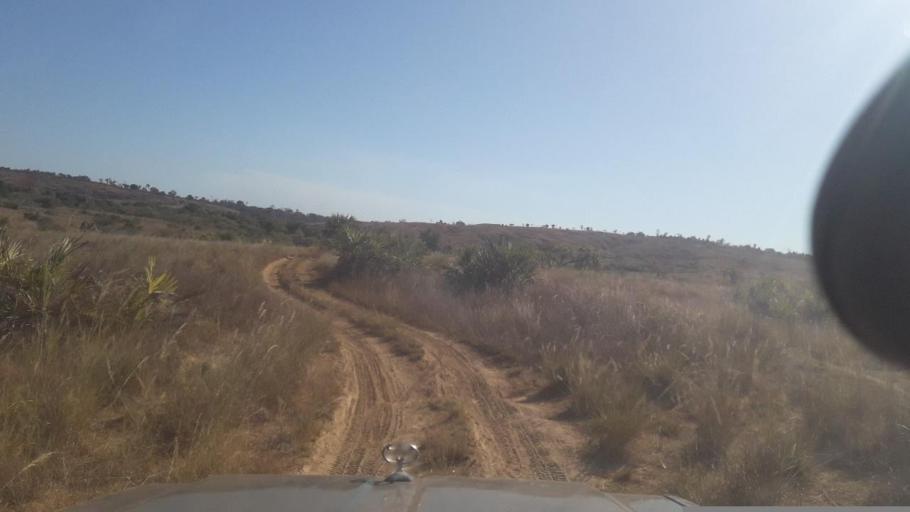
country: MG
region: Boeny
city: Sitampiky
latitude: -16.3752
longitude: 45.5919
